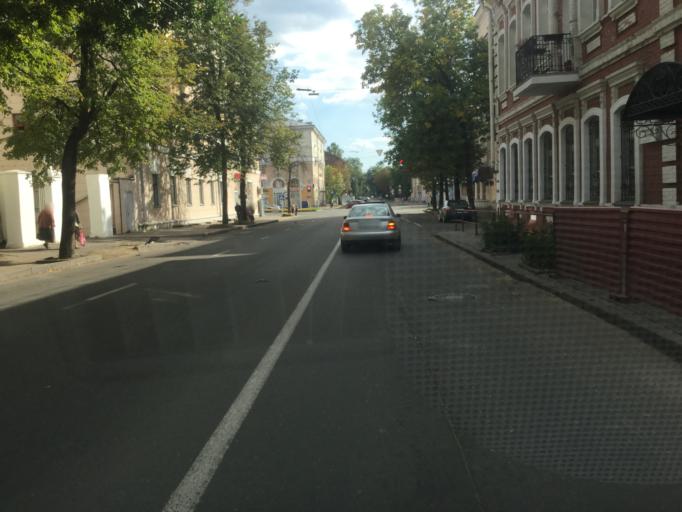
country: BY
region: Vitebsk
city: Vitebsk
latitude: 55.1946
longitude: 30.1952
